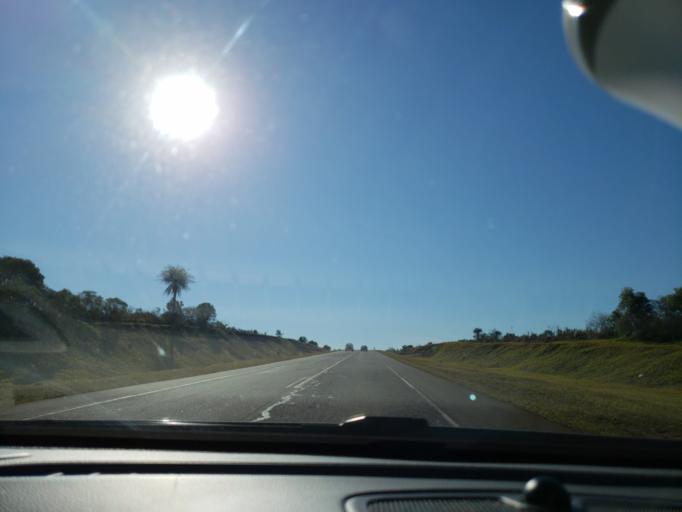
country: AR
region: Misiones
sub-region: Departamento de Apostoles
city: Apostoles
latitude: -27.8424
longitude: -55.7666
